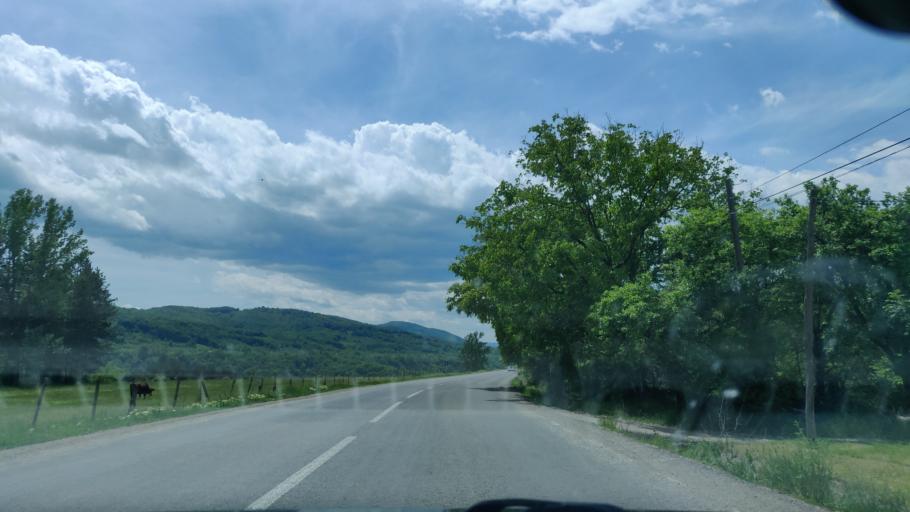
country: RO
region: Vrancea
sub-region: Comuna Vidra
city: Vidra
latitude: 45.8969
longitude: 26.8639
